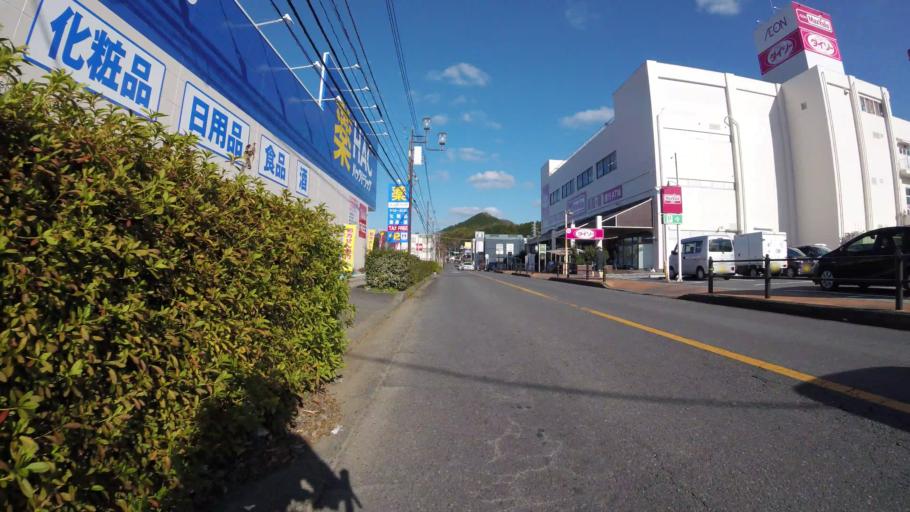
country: JP
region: Shizuoka
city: Ito
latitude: 34.9810
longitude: 138.9516
